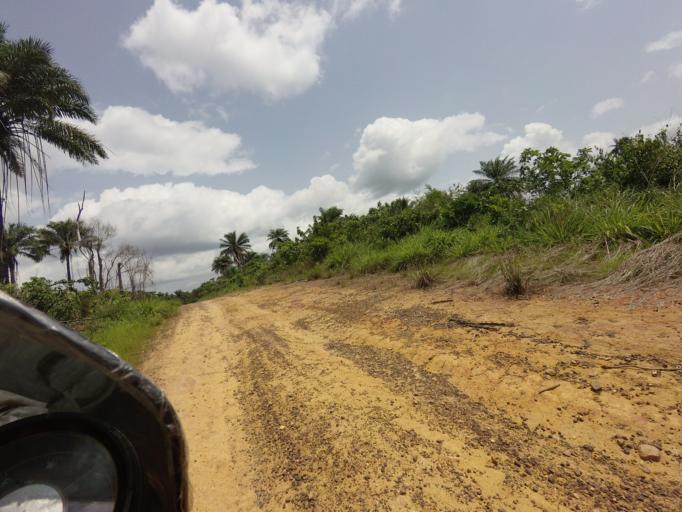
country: SL
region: Eastern Province
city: Kailahun
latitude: 8.3494
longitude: -10.7135
